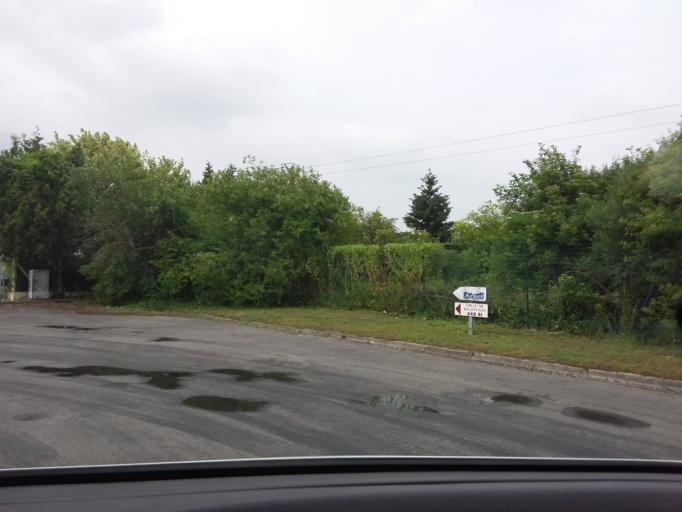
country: FR
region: Picardie
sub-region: Departement de l'Aisne
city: Laon
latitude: 49.5875
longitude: 3.6445
